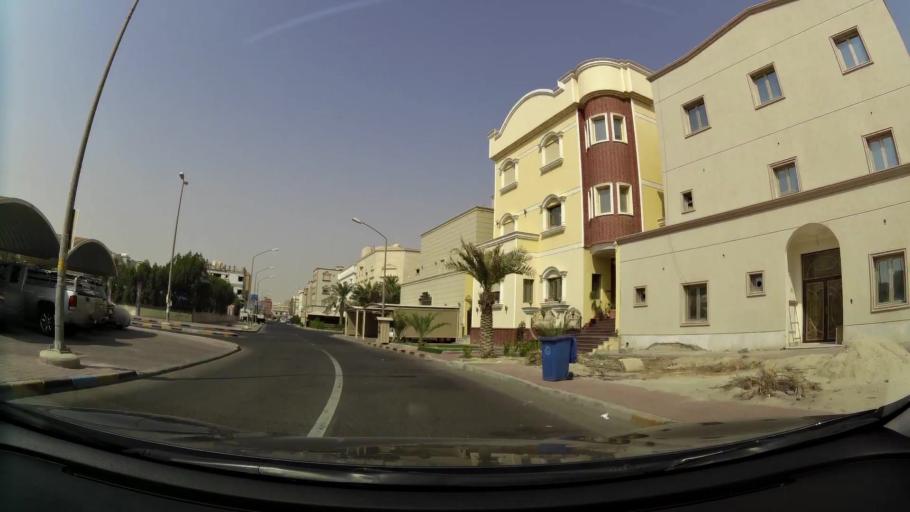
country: KW
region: Muhafazat al Jahra'
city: Al Jahra'
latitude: 29.3242
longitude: 47.7417
